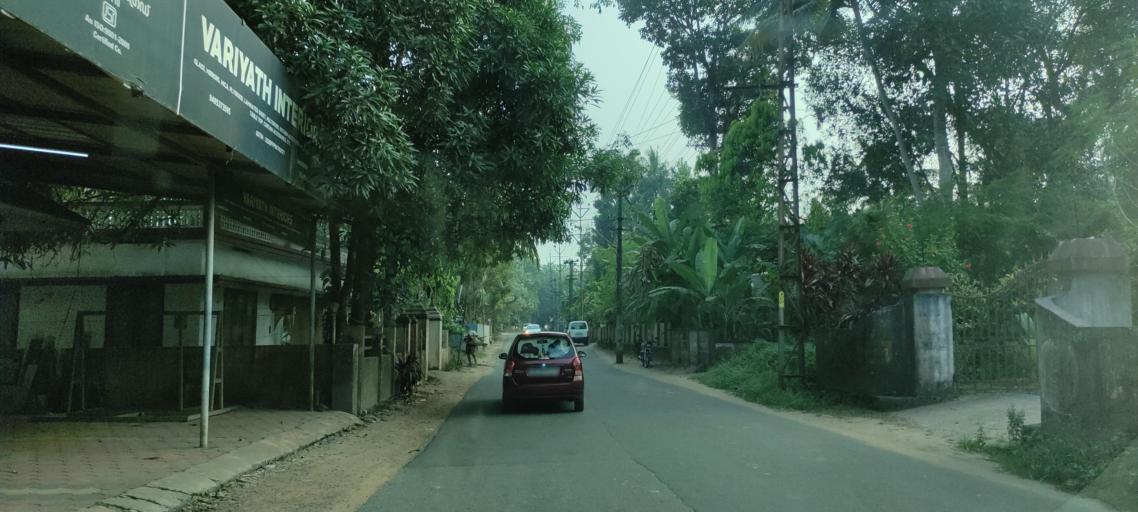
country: IN
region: Kerala
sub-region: Kottayam
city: Vaikam
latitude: 9.7140
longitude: 76.4756
